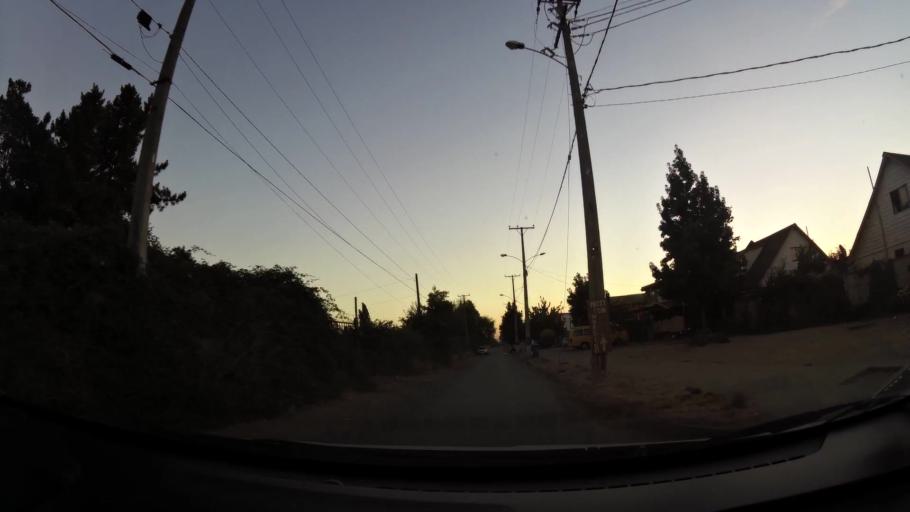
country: CL
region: Maule
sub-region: Provincia de Talca
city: Talca
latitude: -35.4482
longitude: -71.6242
